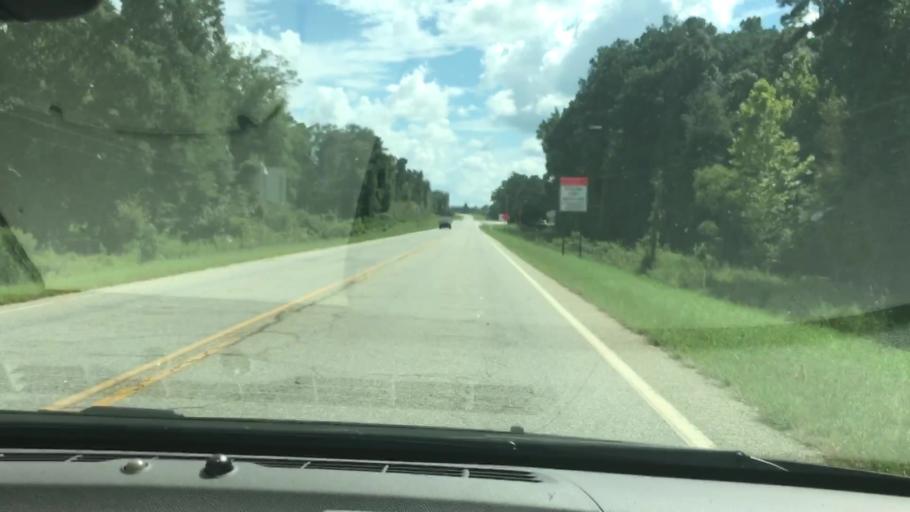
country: US
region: Georgia
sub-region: Clay County
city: Fort Gaines
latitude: 31.6838
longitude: -85.0470
